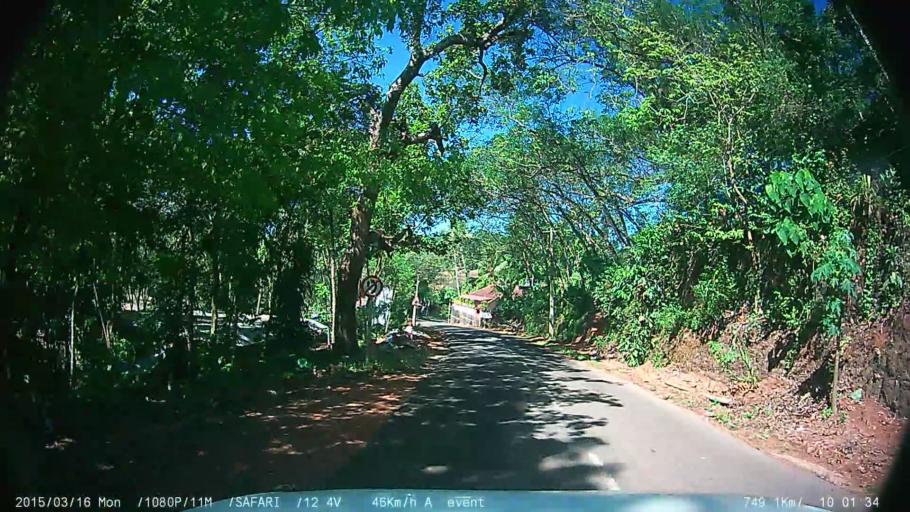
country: IN
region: Kerala
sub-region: Kottayam
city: Palackattumala
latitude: 9.7818
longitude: 76.5828
